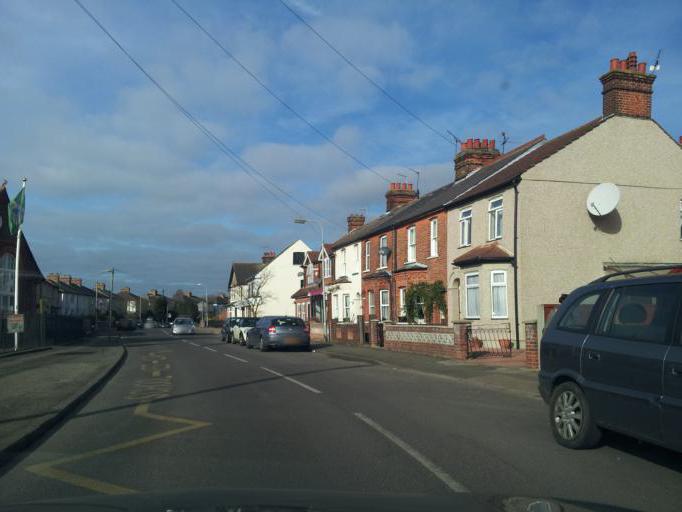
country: GB
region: England
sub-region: Hertfordshire
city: St Albans
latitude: 51.7470
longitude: -0.3091
